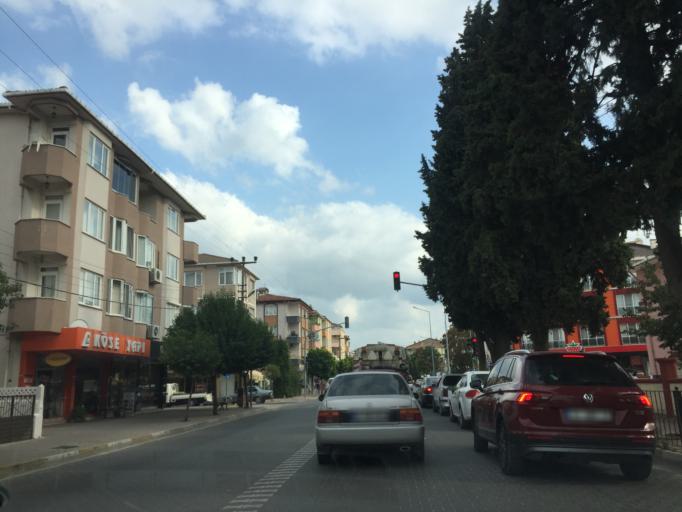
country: TR
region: Balikesir
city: Gonen
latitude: 40.1062
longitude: 27.6549
